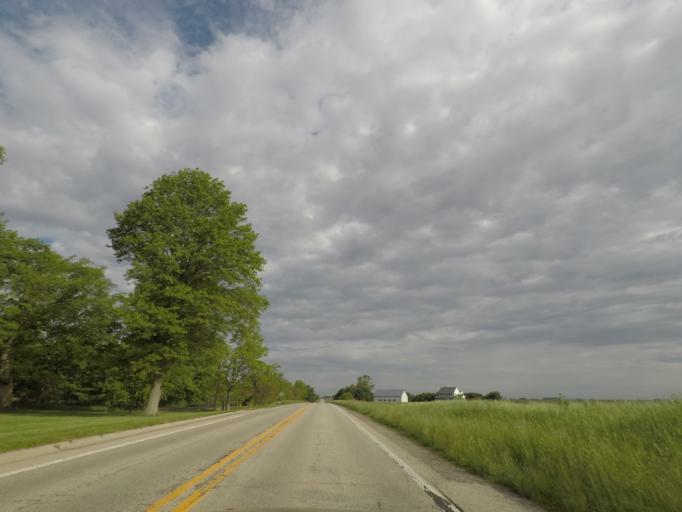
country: US
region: Illinois
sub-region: Logan County
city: Mount Pulaski
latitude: 40.0644
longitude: -89.2863
